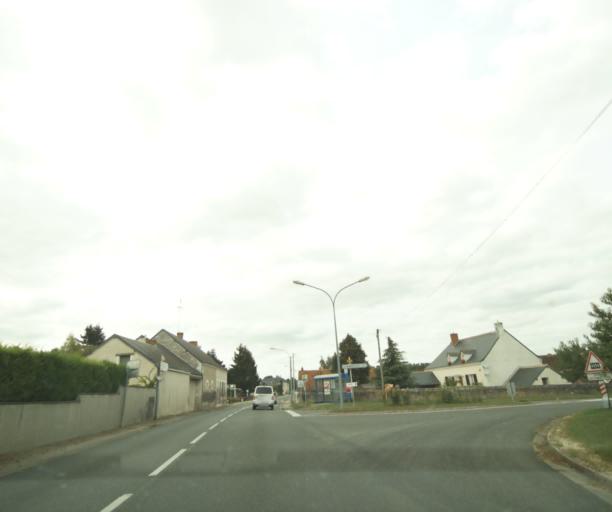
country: FR
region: Centre
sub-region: Departement d'Indre-et-Loire
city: Perrusson
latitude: 47.0593
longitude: 1.0840
